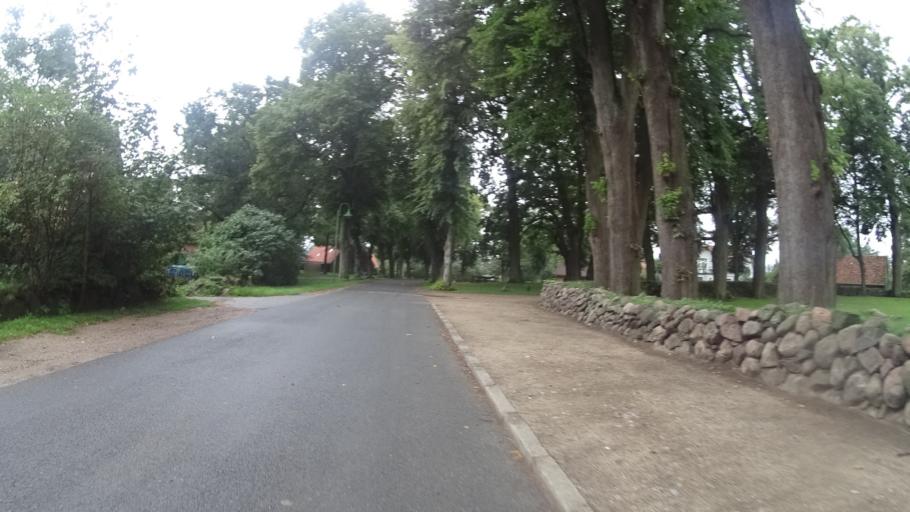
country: DE
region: Schleswig-Holstein
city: Siebeneichen
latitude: 53.5111
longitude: 10.6188
